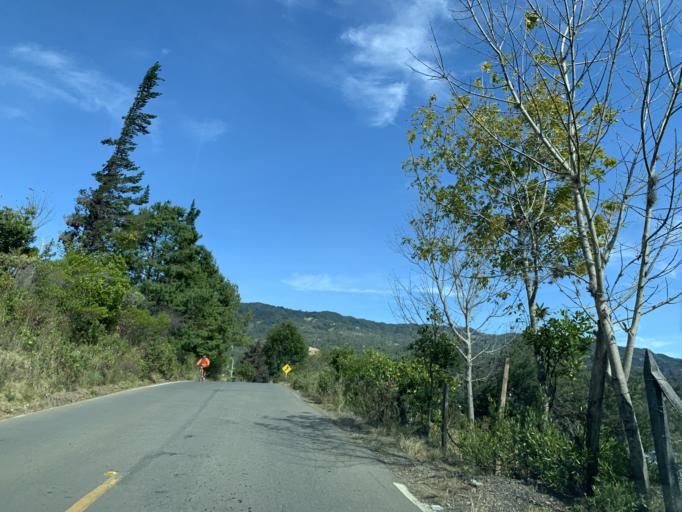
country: CO
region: Boyaca
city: Santa Sofia
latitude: 5.7053
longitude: -73.5933
